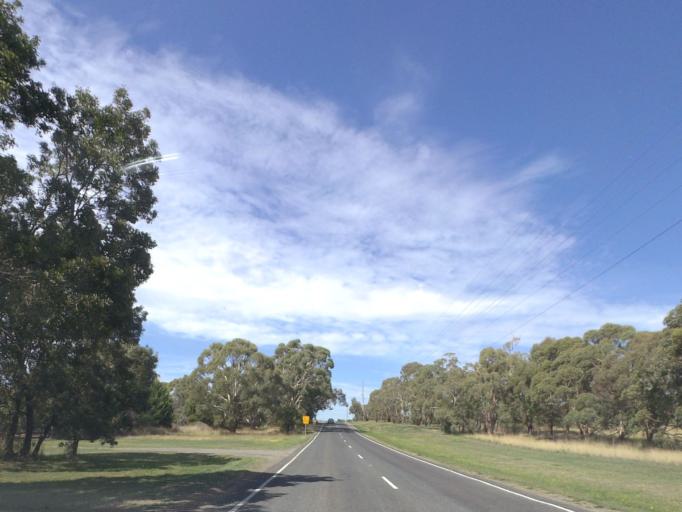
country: AU
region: Victoria
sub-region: Mount Alexander
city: Castlemaine
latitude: -37.2592
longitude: 144.4767
